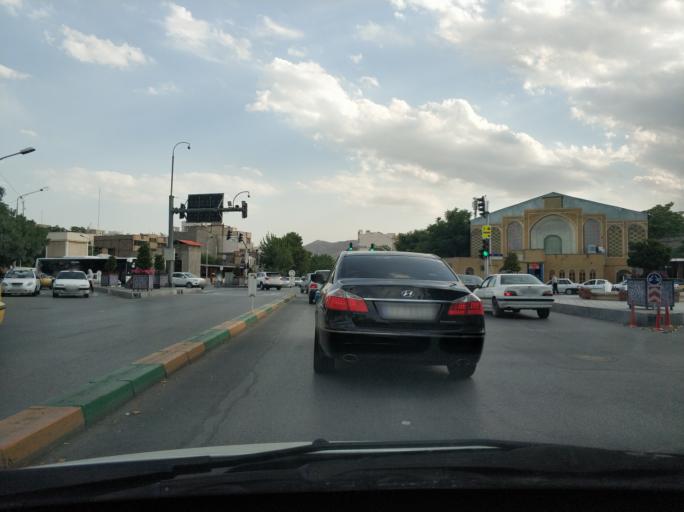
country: IR
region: Razavi Khorasan
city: Mashhad
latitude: 36.2817
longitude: 59.5961
